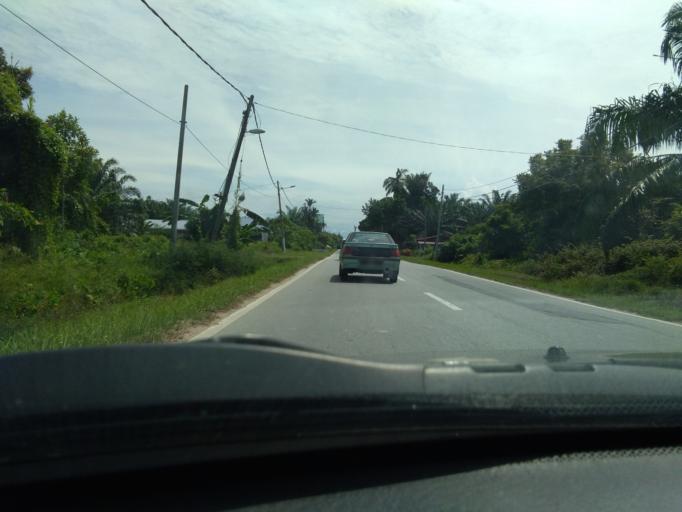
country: MY
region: Perak
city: Bagan Serai
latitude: 5.0242
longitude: 100.5521
